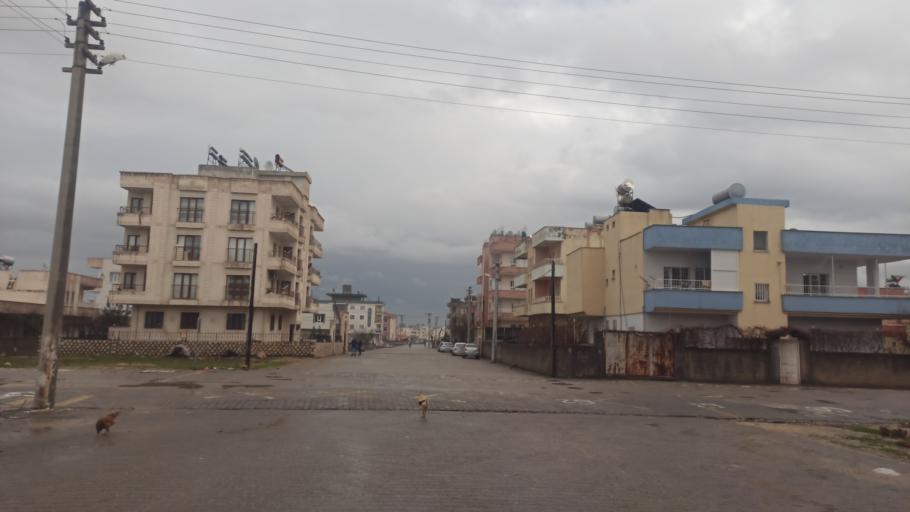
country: TR
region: Mardin
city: Midyat
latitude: 37.4236
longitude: 41.3546
